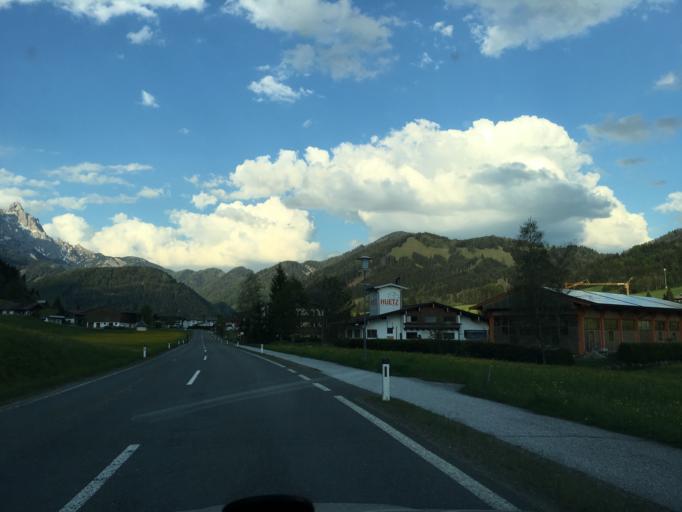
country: AT
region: Tyrol
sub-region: Politischer Bezirk Kitzbuhel
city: Fieberbrunn
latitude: 47.5012
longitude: 12.5644
